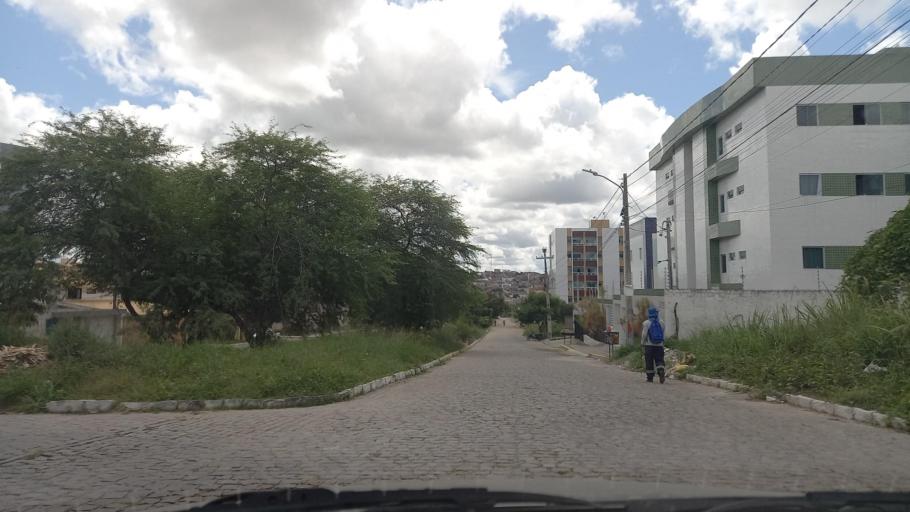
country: BR
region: Pernambuco
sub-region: Caruaru
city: Caruaru
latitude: -8.2920
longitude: -35.9547
